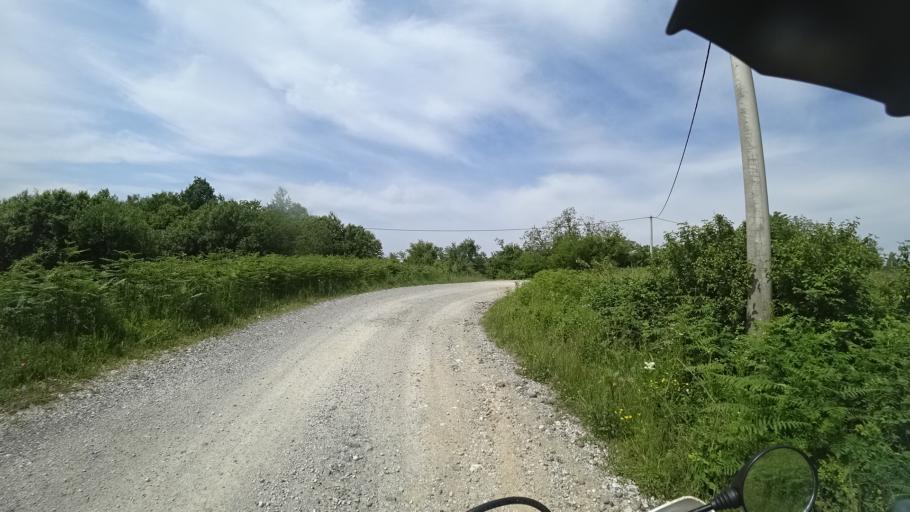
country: HR
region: Sisacko-Moslavacka
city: Gvozd
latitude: 45.3914
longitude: 15.8521
